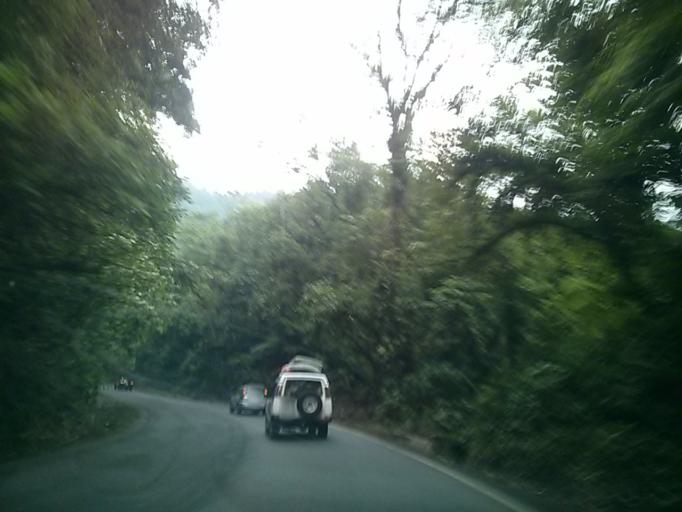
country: CR
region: San Jose
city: Dulce Nombre de Jesus
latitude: 10.1291
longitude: -83.9695
